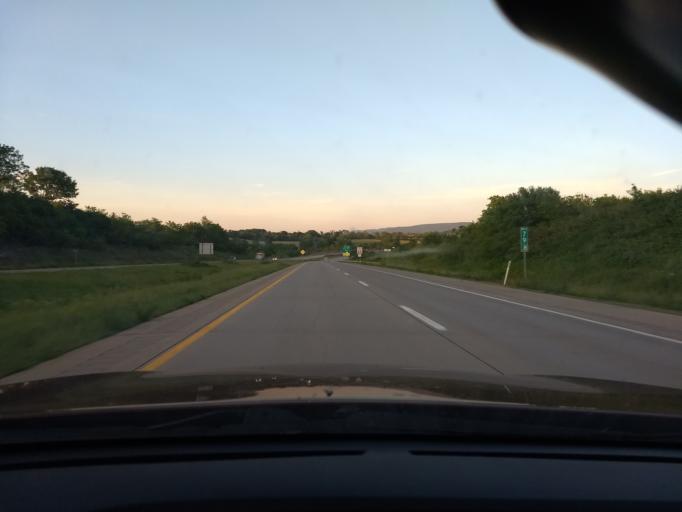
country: US
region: Pennsylvania
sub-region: Centre County
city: Pleasant Gap
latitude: 40.8786
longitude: -77.7672
